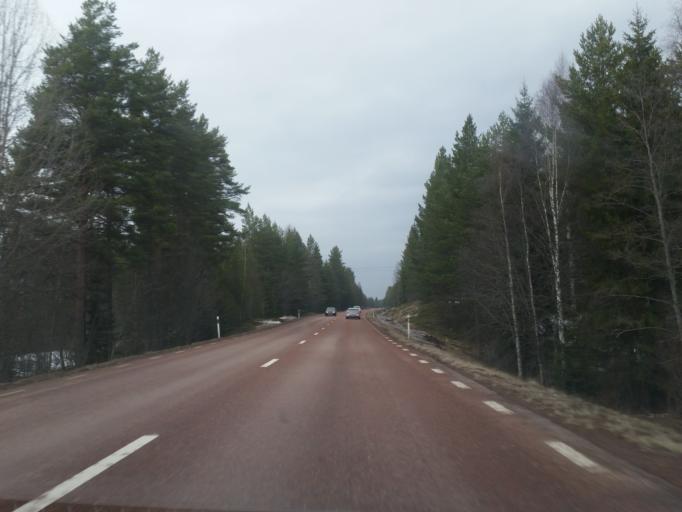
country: SE
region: Dalarna
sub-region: Alvdalens Kommun
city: AElvdalen
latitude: 61.1296
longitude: 14.1846
